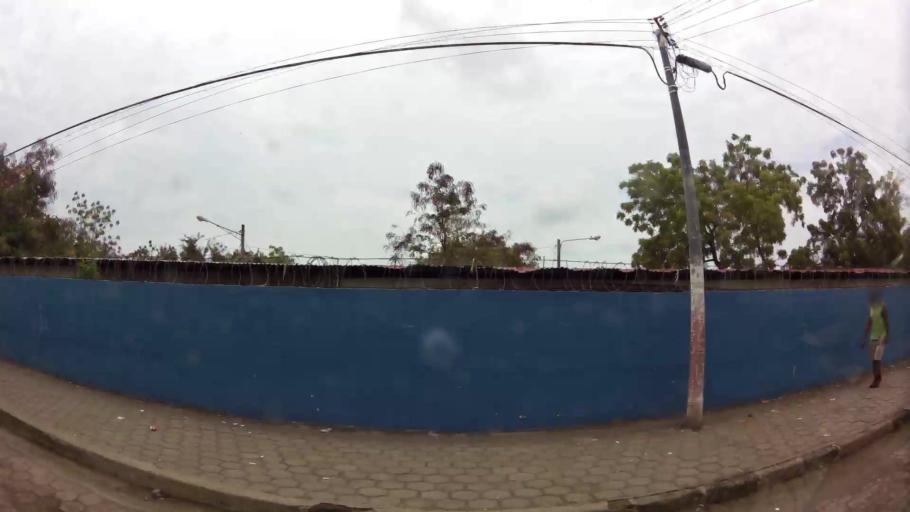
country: NI
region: Granada
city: Granada
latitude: 11.9170
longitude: -85.9550
